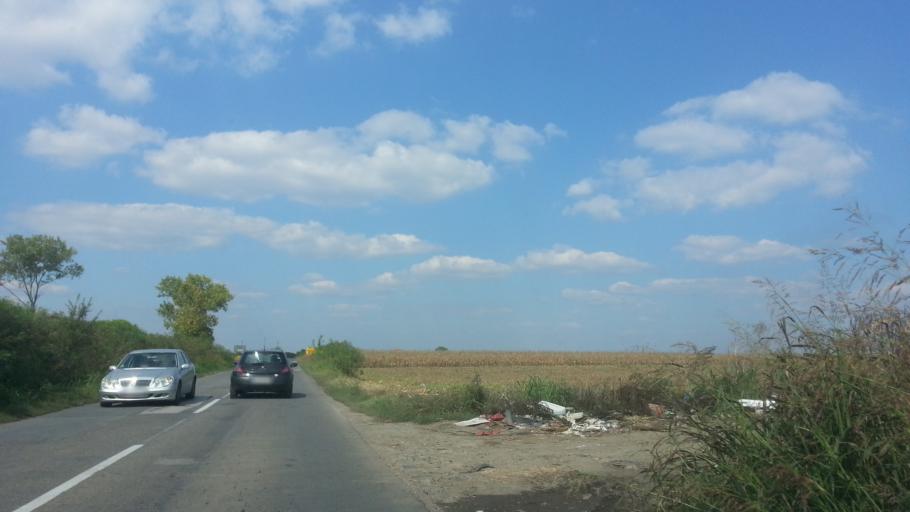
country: RS
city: Novi Banovci
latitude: 44.9232
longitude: 20.2813
